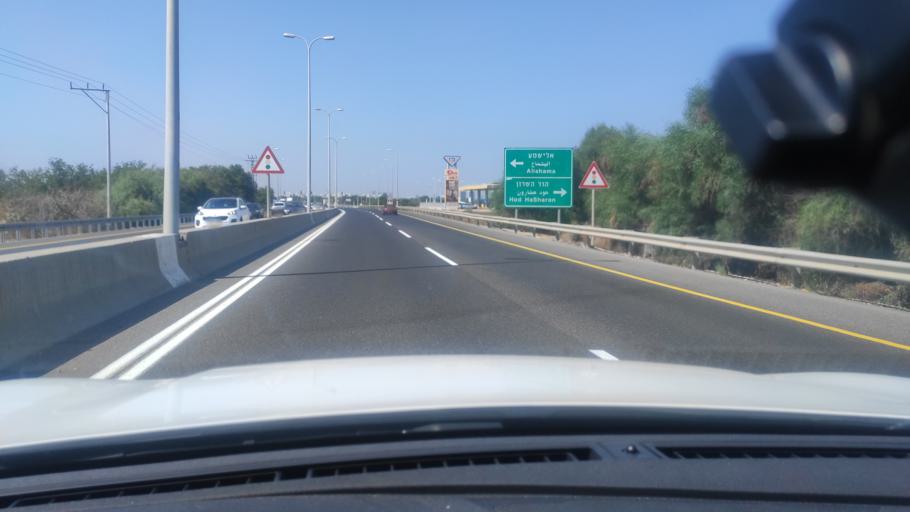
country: IL
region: Central District
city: Kfar Saba
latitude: 32.1539
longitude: 34.9231
